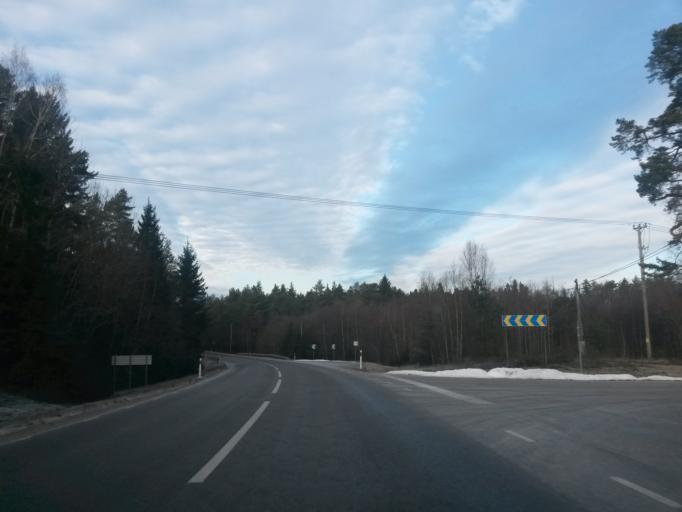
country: SE
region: Vaestra Goetaland
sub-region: Vargarda Kommun
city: Vargarda
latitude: 57.9082
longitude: 12.9062
